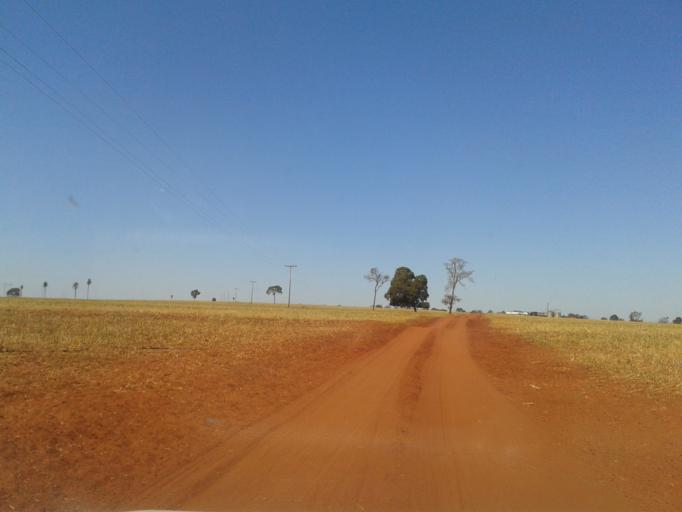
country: BR
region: Minas Gerais
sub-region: Santa Vitoria
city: Santa Vitoria
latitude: -19.2271
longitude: -50.2104
